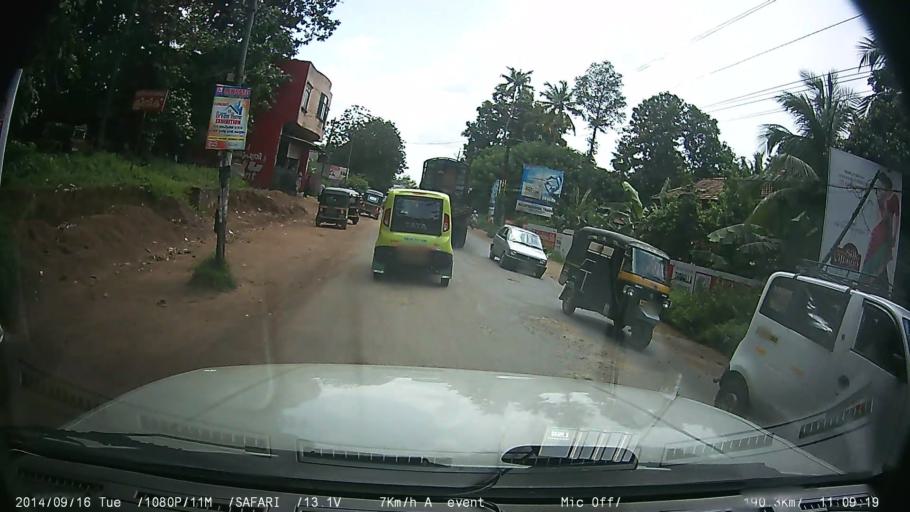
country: IN
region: Kerala
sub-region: Kottayam
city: Kottayam
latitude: 9.5262
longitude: 76.5219
